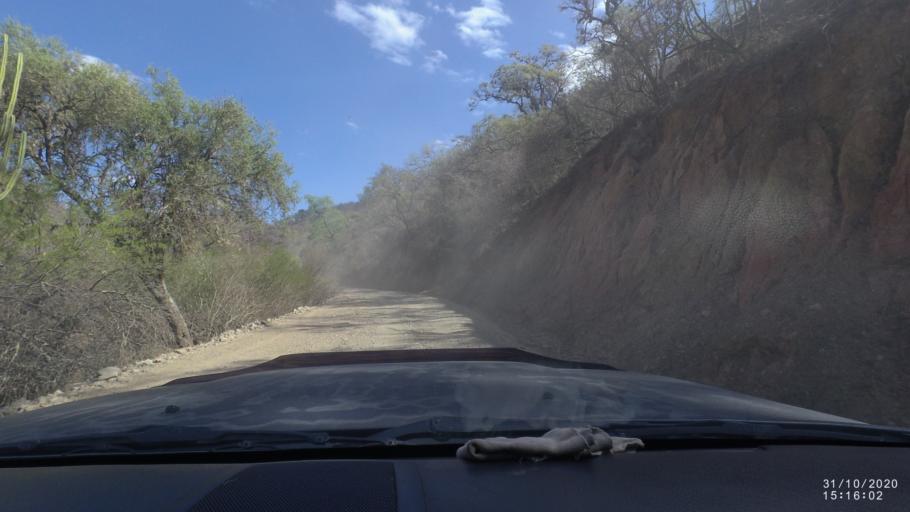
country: BO
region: Cochabamba
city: Aiquile
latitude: -18.3328
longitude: -64.7737
